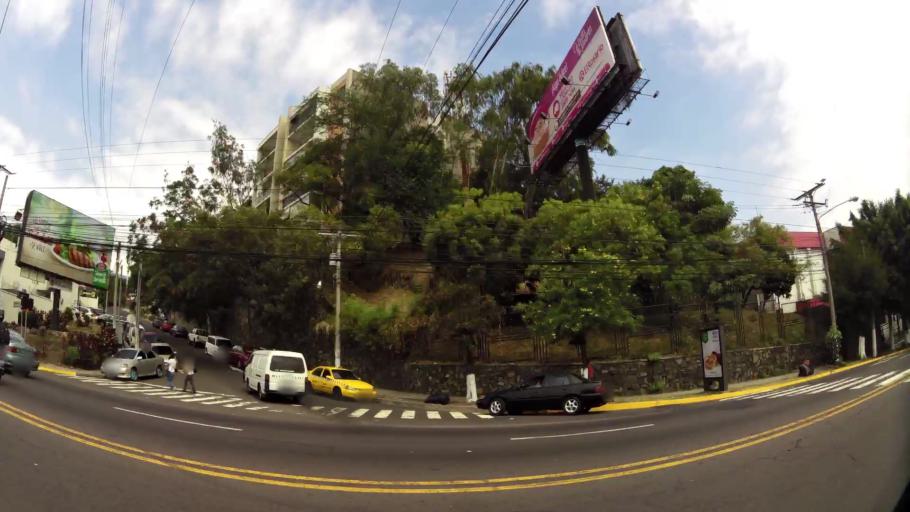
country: SV
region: La Libertad
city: Antiguo Cuscatlan
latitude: 13.7031
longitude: -89.2447
